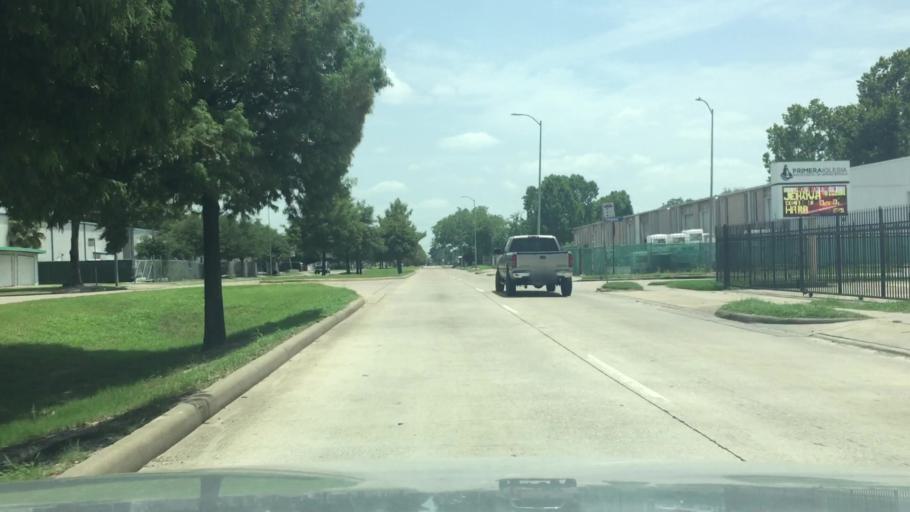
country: US
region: Texas
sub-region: Harris County
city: Jersey Village
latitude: 29.8466
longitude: -95.5452
